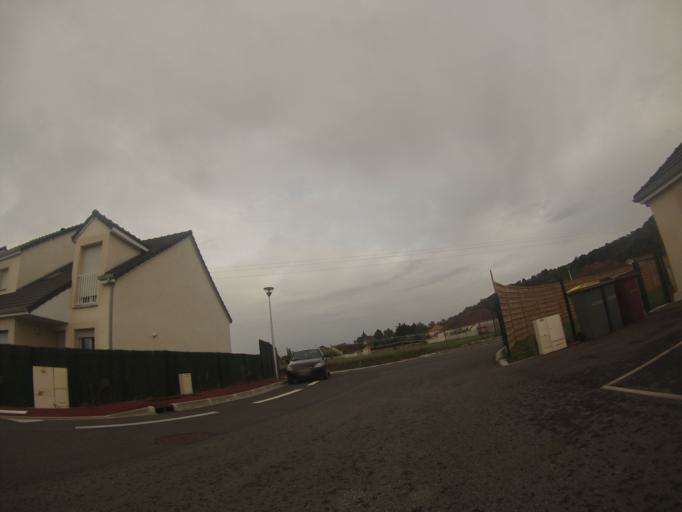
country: FR
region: Aquitaine
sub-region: Departement des Pyrenees-Atlantiques
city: Bizanos
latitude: 43.2764
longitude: -0.3552
